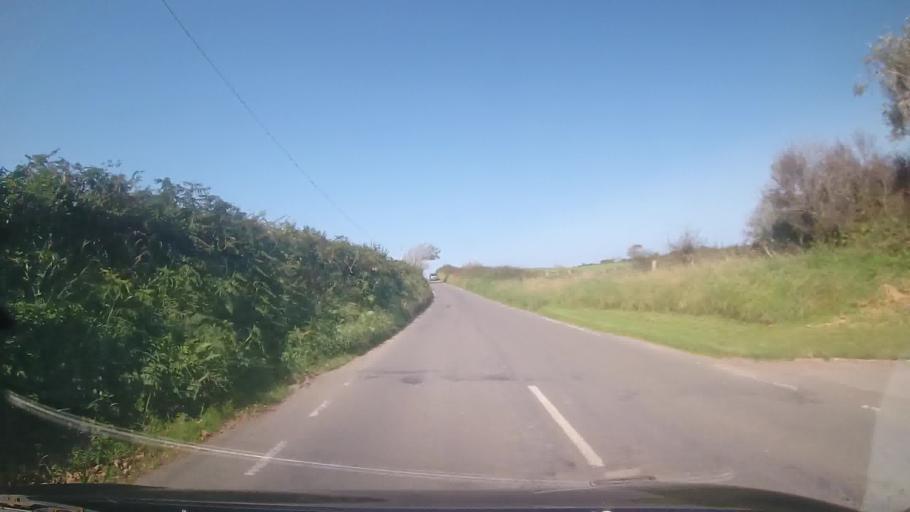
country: GB
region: Wales
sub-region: Pembrokeshire
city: Camrose
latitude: 51.8578
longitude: -5.0138
